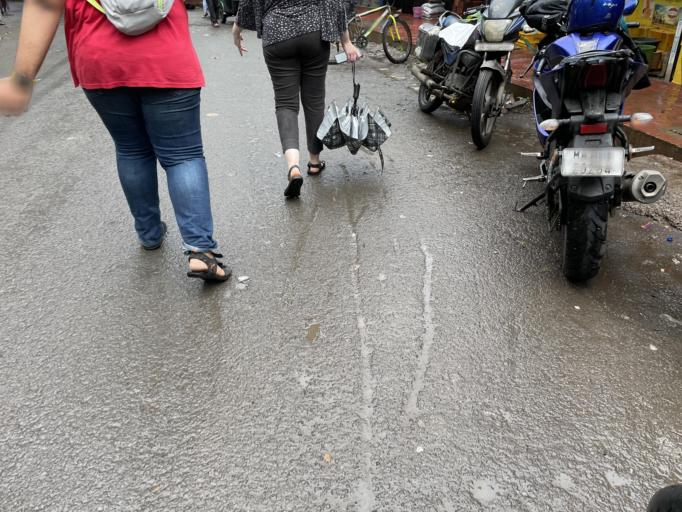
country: IN
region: Maharashtra
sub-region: Mumbai Suburban
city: Borivli
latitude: 19.2539
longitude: 72.8622
